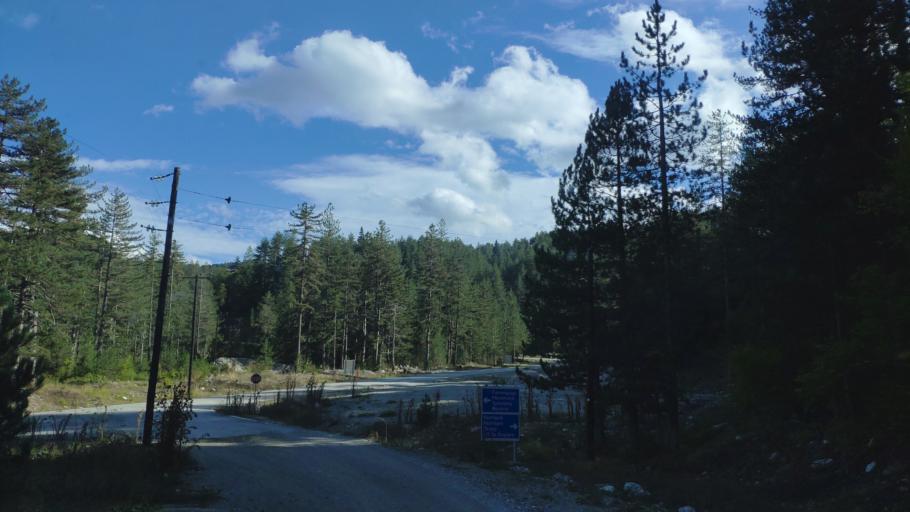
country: AL
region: Korce
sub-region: Rrethi i Devollit
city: Miras
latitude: 40.4116
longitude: 20.8734
